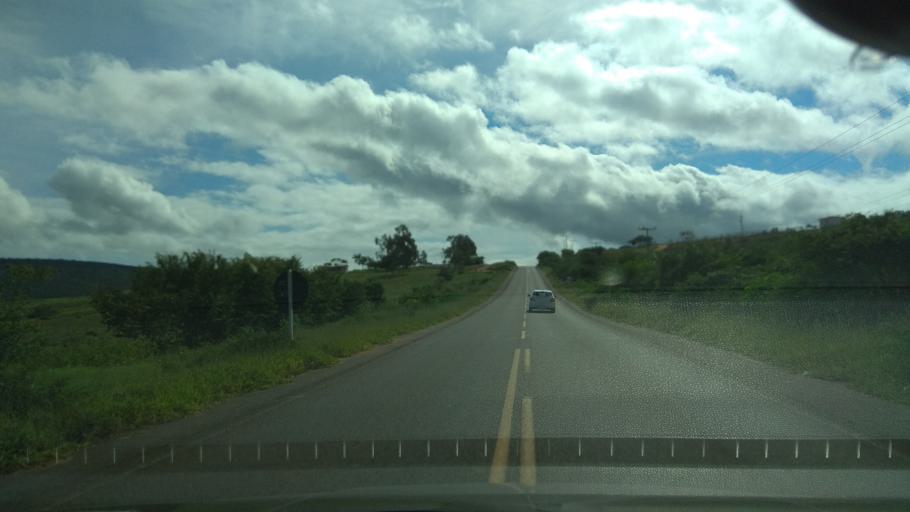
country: BR
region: Bahia
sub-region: Jaguaquara
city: Jaguaquara
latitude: -13.4425
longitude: -39.9345
